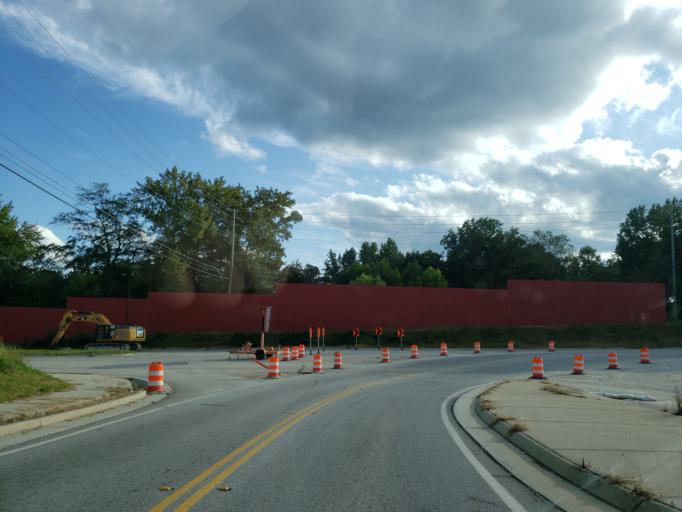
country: US
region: Georgia
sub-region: Douglas County
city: Douglasville
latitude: 33.7567
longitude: -84.7340
